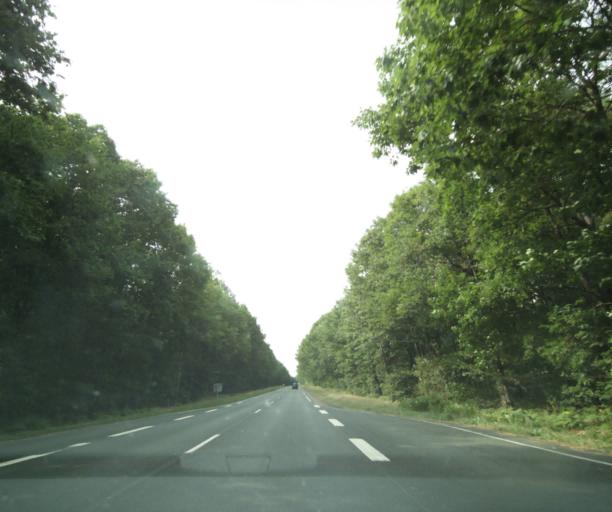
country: FR
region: Pays de la Loire
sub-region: Departement de la Sarthe
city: Marigne-Laille
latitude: 47.7667
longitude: 0.3518
